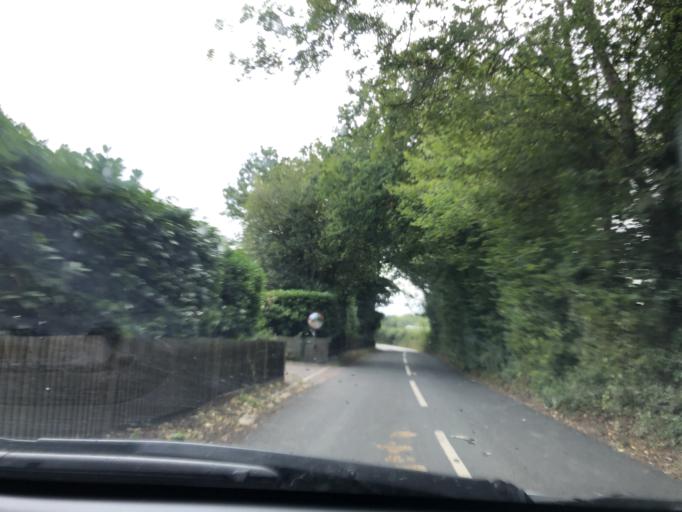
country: GB
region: England
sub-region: Kent
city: Edenbridge
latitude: 51.2256
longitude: 0.0916
